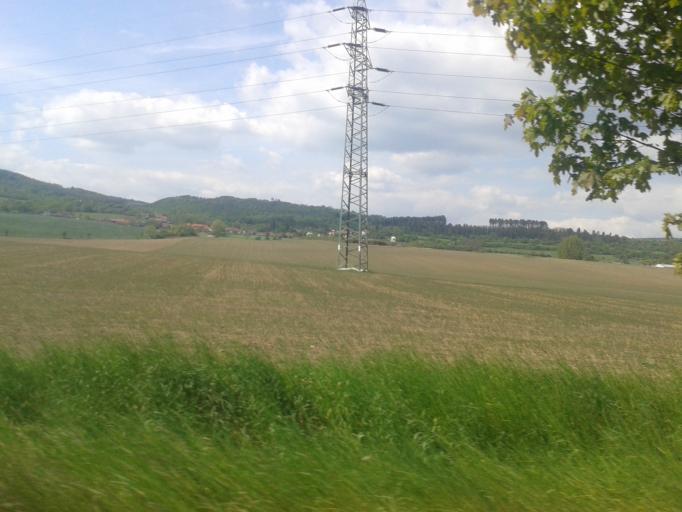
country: CZ
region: Central Bohemia
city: Zdice
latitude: 49.9204
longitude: 13.9867
